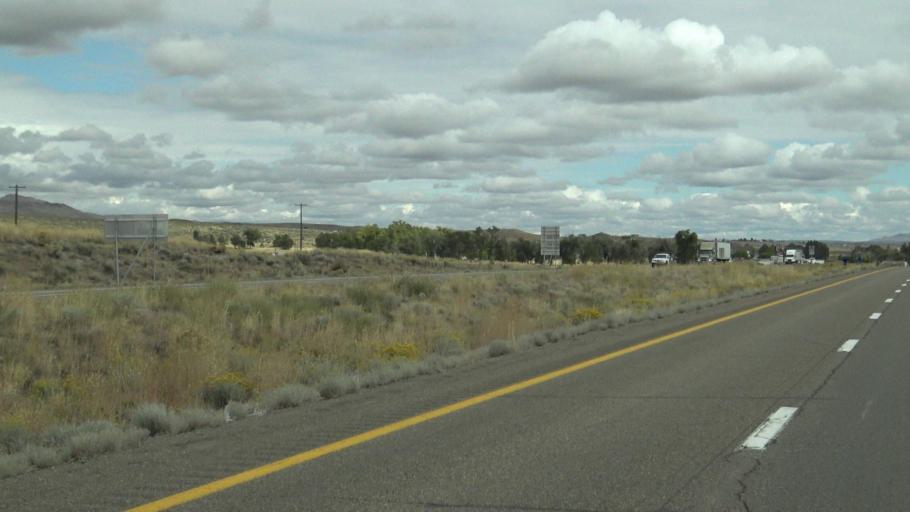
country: US
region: Nevada
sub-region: Elko County
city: Elko
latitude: 40.8771
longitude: -115.7204
